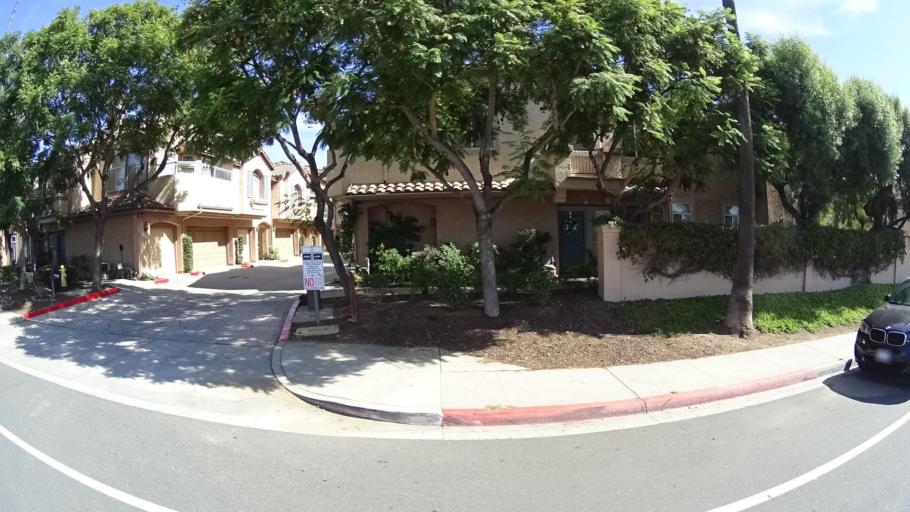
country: US
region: California
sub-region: San Diego County
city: Rancho San Diego
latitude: 32.7457
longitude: -116.9357
